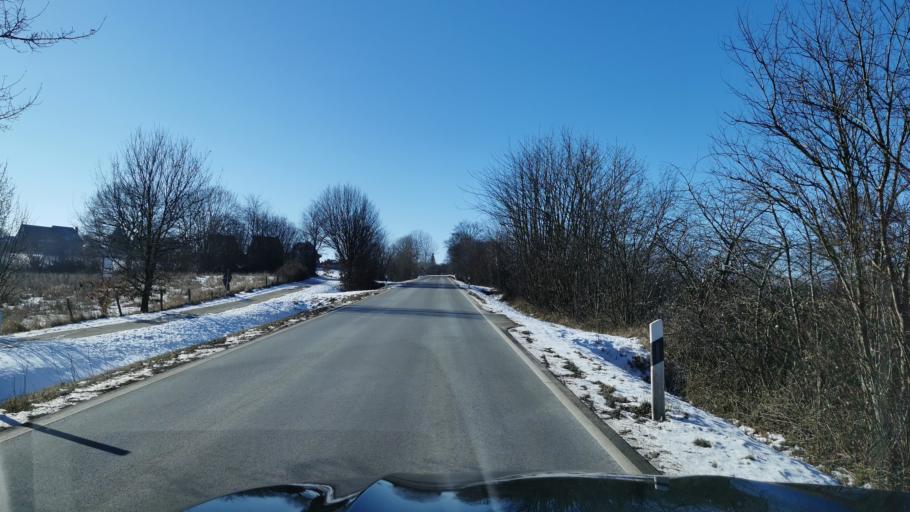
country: DE
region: Schleswig-Holstein
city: Westerholz
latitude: 54.8181
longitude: 9.6475
